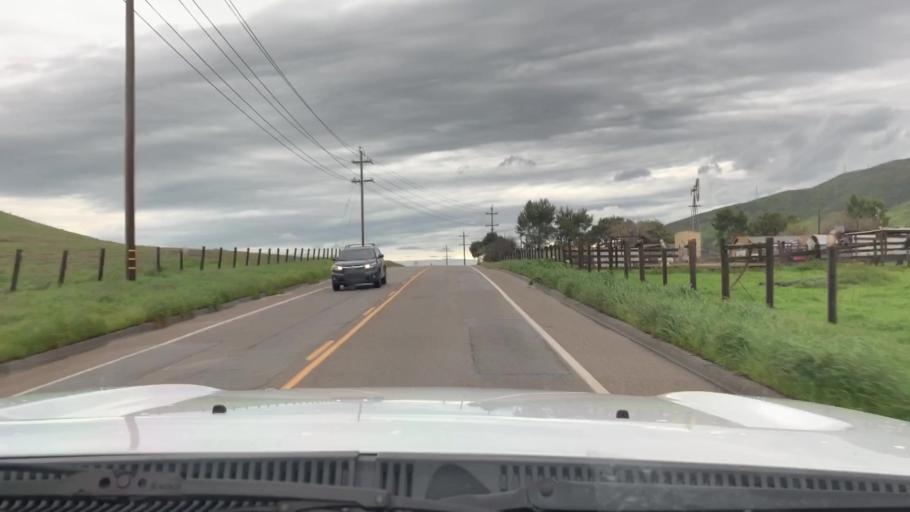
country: US
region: California
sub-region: San Luis Obispo County
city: San Luis Obispo
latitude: 35.2529
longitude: -120.6273
